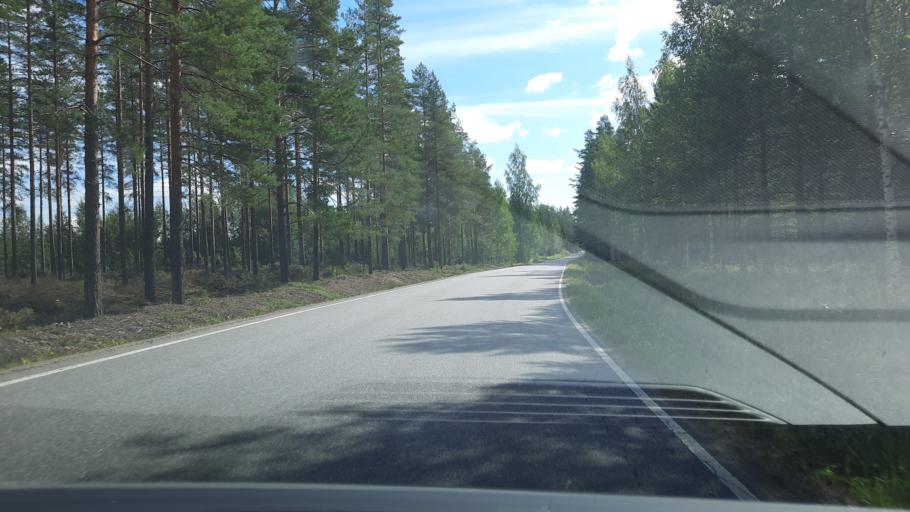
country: FI
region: Pirkanmaa
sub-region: Etelae-Pirkanmaa
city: Urjala
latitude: 61.1703
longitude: 23.3986
